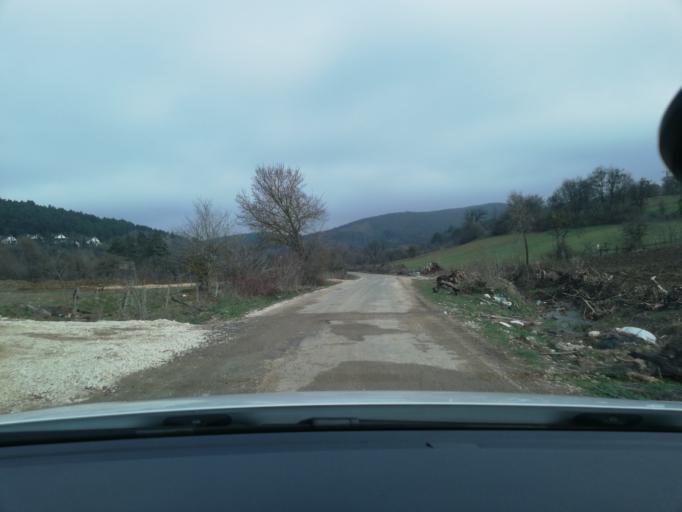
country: TR
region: Bolu
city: Bolu
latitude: 40.6728
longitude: 31.4724
